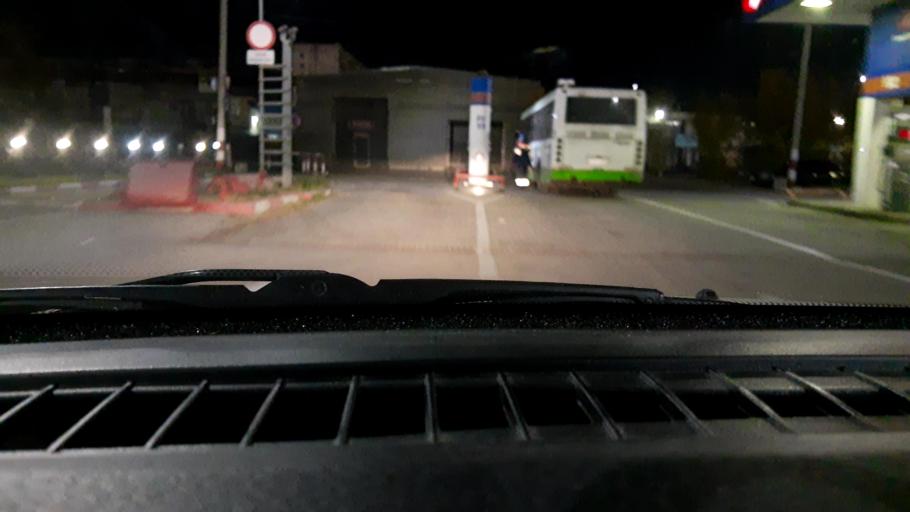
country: RU
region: Nizjnij Novgorod
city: Nizhniy Novgorod
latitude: 56.2583
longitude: 43.8897
